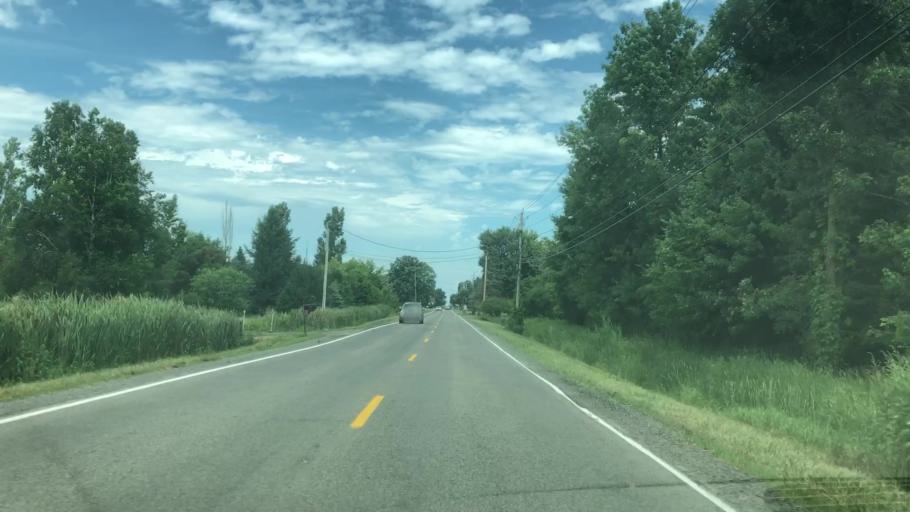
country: US
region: New York
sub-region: Monroe County
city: Webster
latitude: 43.1781
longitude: -77.4004
